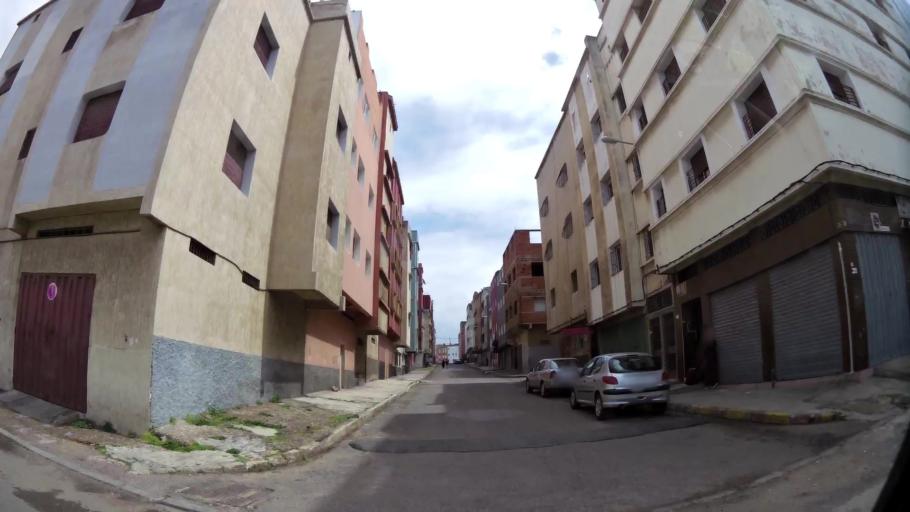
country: MA
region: Grand Casablanca
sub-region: Mediouna
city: Tit Mellil
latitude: 33.6032
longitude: -7.5166
